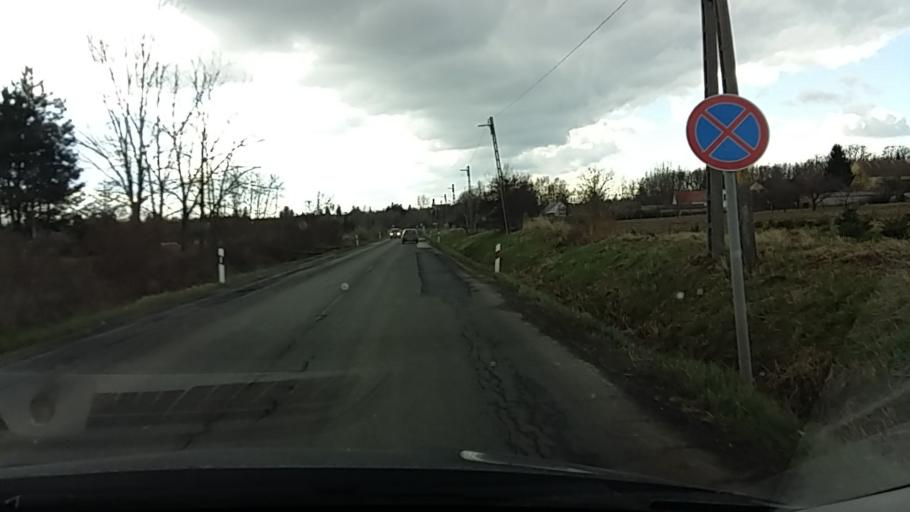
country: HU
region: Somogy
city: Bohonye
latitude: 46.4170
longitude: 17.3828
